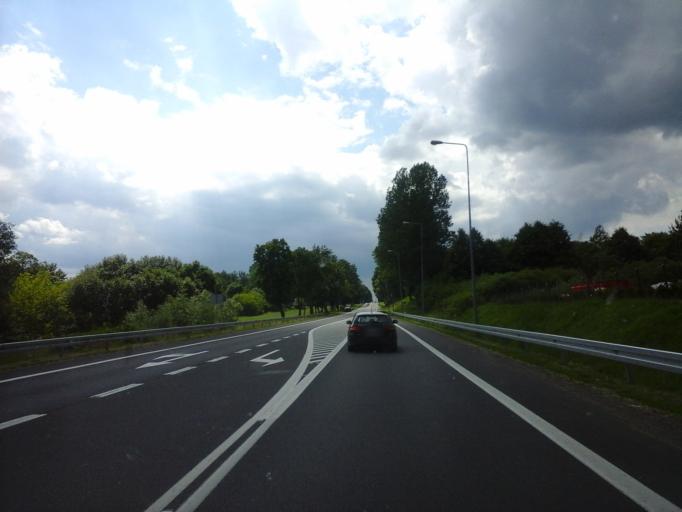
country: PL
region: West Pomeranian Voivodeship
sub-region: Powiat bialogardzki
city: Karlino
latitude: 54.0254
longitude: 15.8601
